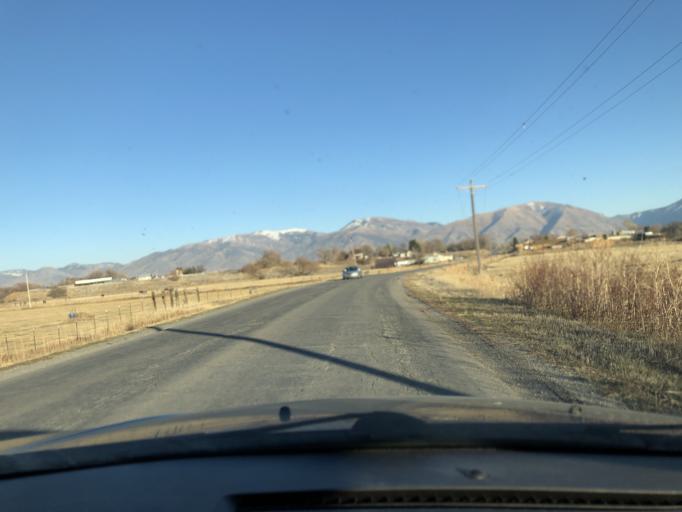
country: US
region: Utah
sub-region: Cache County
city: Wellsville
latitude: 41.6471
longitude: -111.9213
